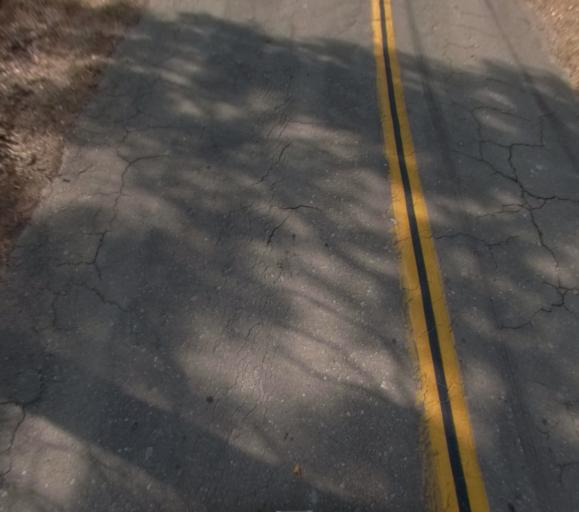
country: US
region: California
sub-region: Madera County
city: Oakhurst
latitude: 37.2556
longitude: -119.5249
